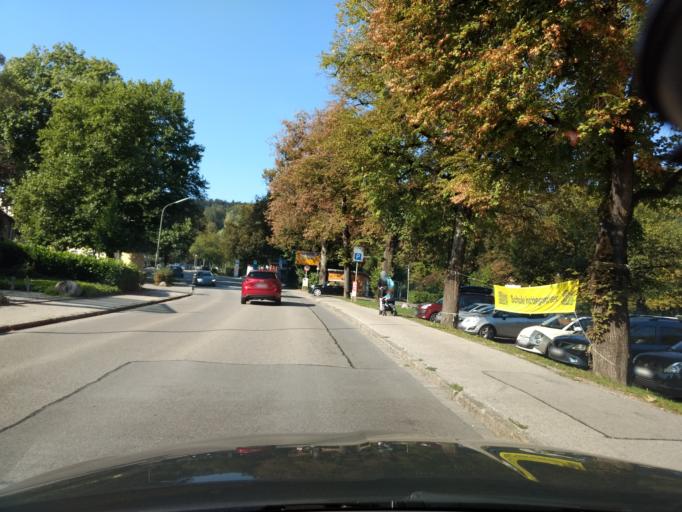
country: DE
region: Bavaria
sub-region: Upper Bavaria
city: Wolfratshausen
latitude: 47.9129
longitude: 11.4213
